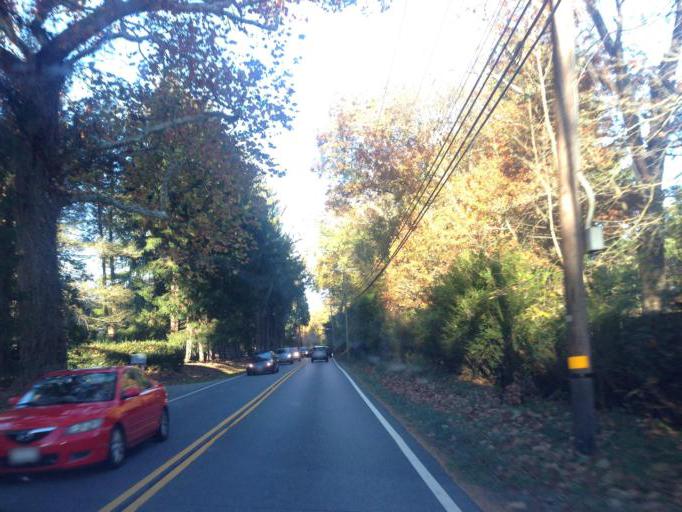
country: US
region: Maryland
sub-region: Baltimore County
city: Mays Chapel
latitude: 39.4219
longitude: -76.6773
